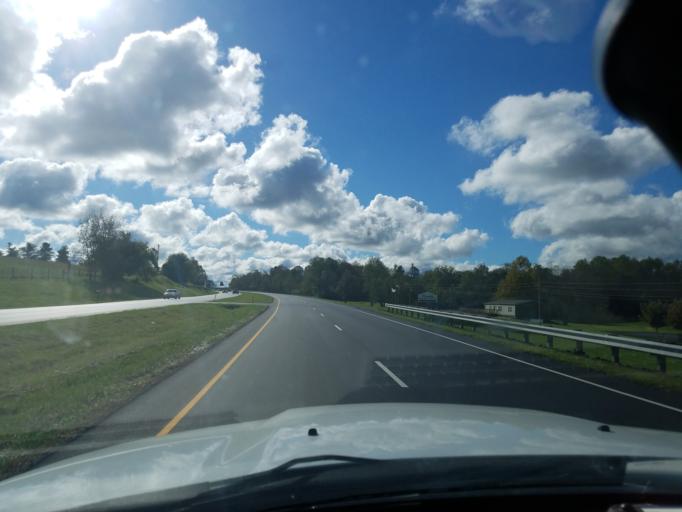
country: US
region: Kentucky
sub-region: Boyle County
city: Junction City
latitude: 37.5948
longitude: -84.7266
